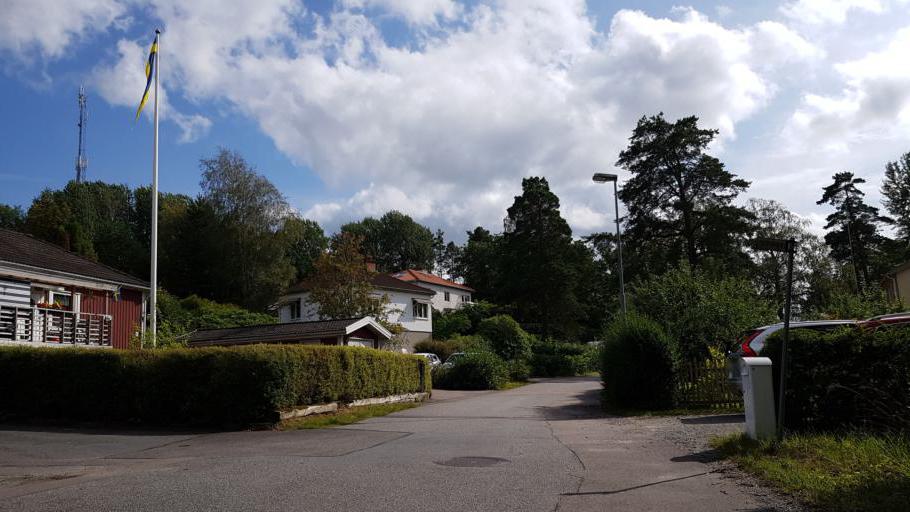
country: SE
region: Vaestra Goetaland
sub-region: Harryda Kommun
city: Molnlycke
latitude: 57.6647
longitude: 12.1082
